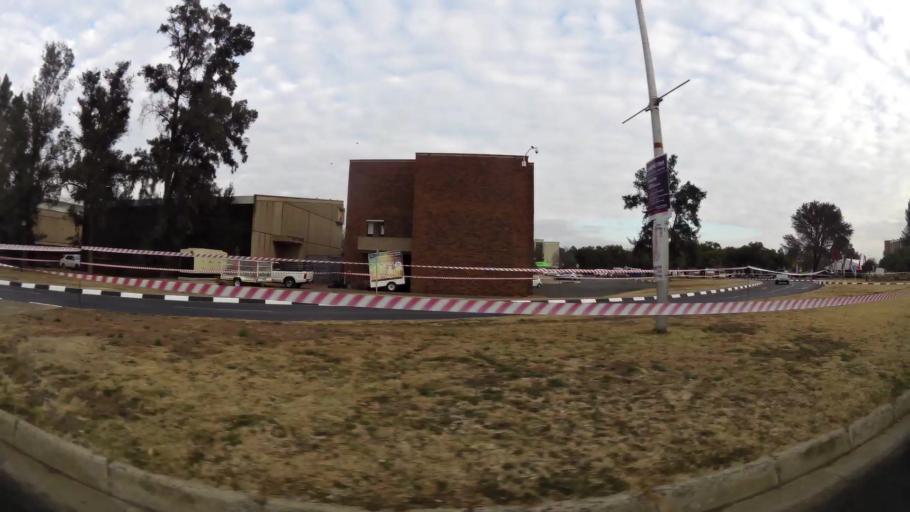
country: ZA
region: Orange Free State
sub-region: Mangaung Metropolitan Municipality
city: Bloemfontein
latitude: -29.1125
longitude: 26.1913
